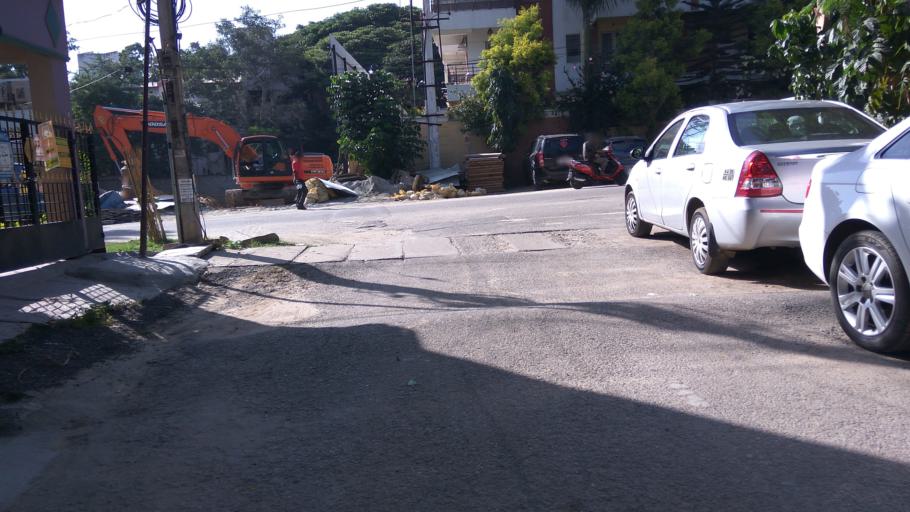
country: IN
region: Karnataka
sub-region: Bangalore Urban
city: Bangalore
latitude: 12.9652
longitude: 77.6355
